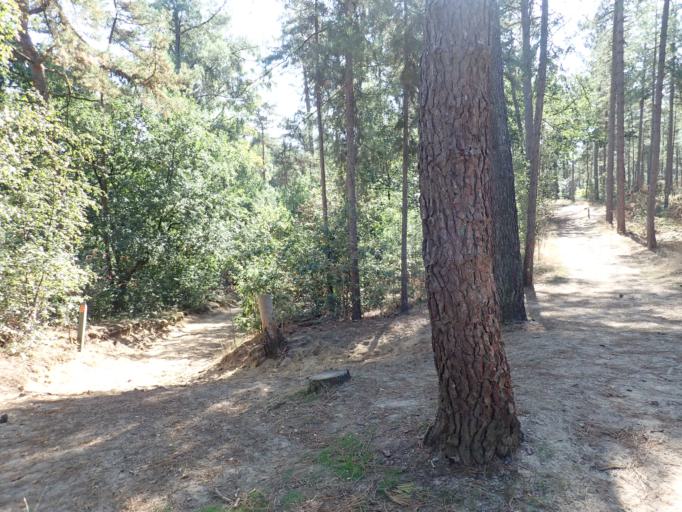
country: BE
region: Flanders
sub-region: Provincie Antwerpen
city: Kasterlee
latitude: 51.2154
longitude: 4.8988
